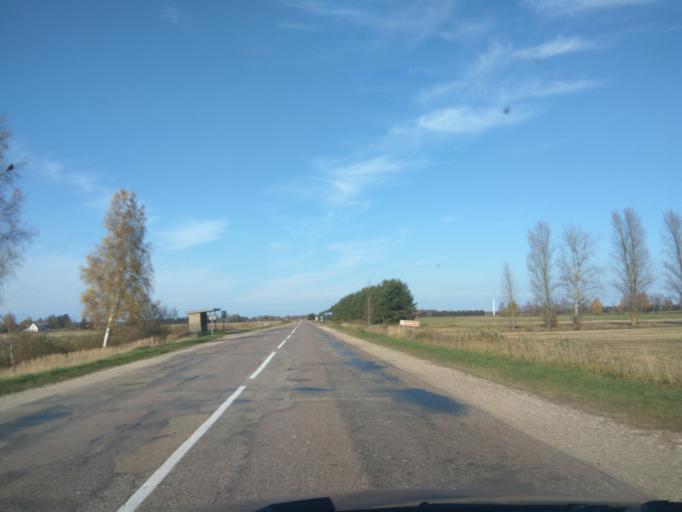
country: LV
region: Ventspils Rajons
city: Piltene
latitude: 57.2531
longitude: 21.5911
